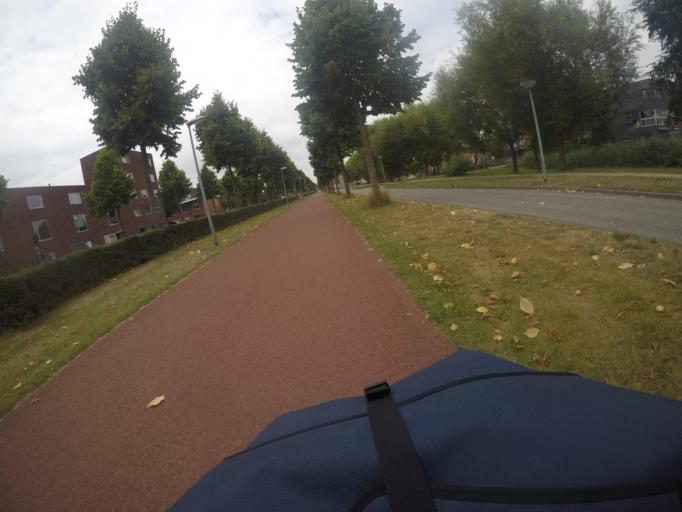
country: NL
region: Flevoland
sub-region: Gemeente Almere
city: Almere Stad
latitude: 52.3853
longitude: 5.1828
